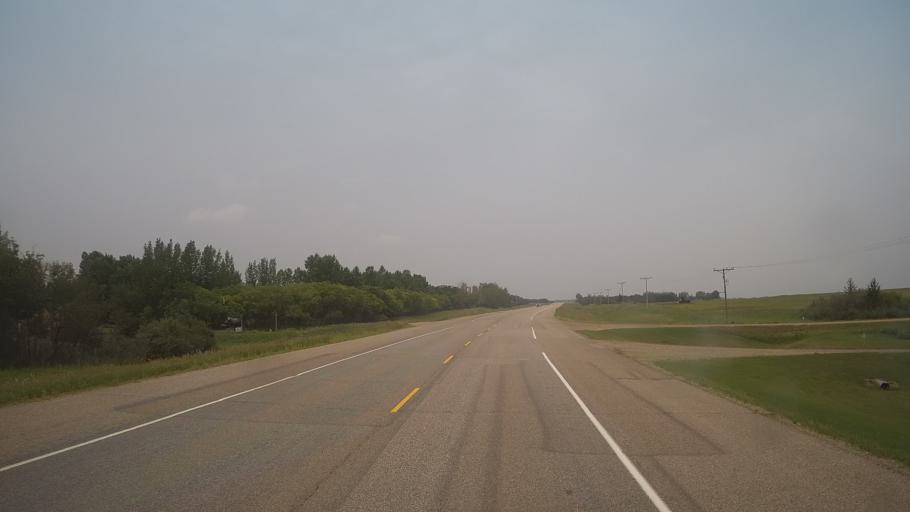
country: CA
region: Saskatchewan
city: Biggar
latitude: 52.0564
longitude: -107.9063
